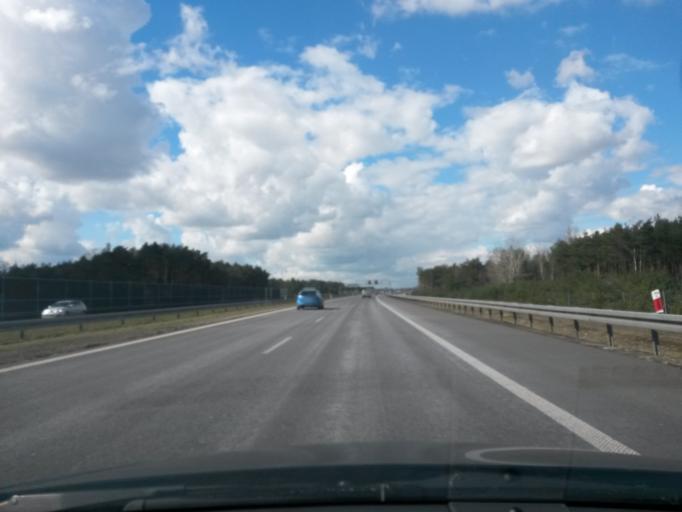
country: PL
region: Greater Poland Voivodeship
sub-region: Powiat kolski
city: Dabie
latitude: 52.0780
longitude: 18.8023
